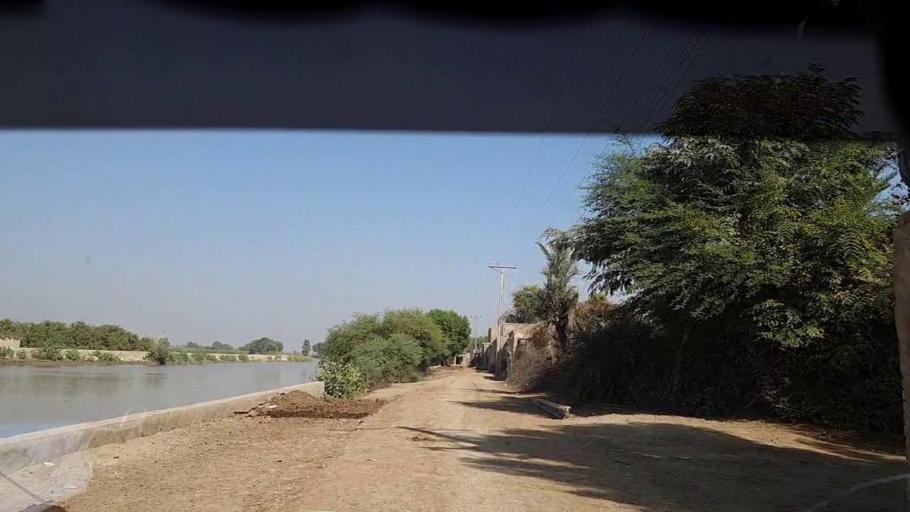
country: PK
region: Sindh
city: Naudero
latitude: 27.6676
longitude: 68.3776
